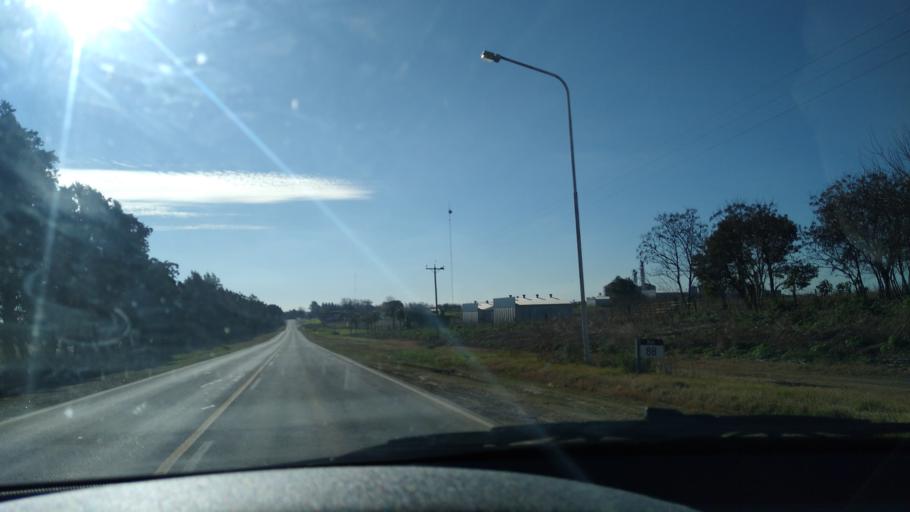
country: AR
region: Entre Rios
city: Aranguren
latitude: -32.4278
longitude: -60.3102
